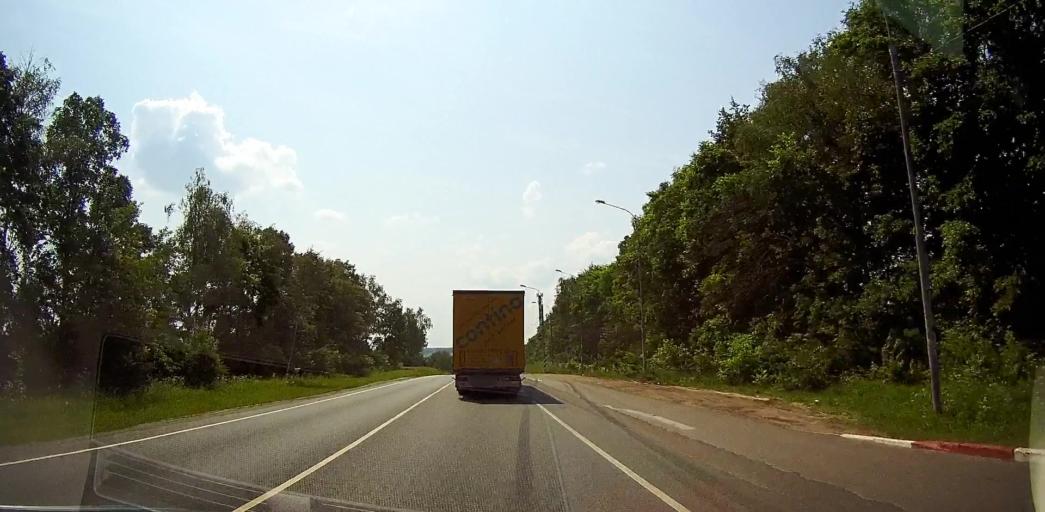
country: RU
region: Moskovskaya
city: Meshcherino
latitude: 55.1991
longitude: 38.3717
